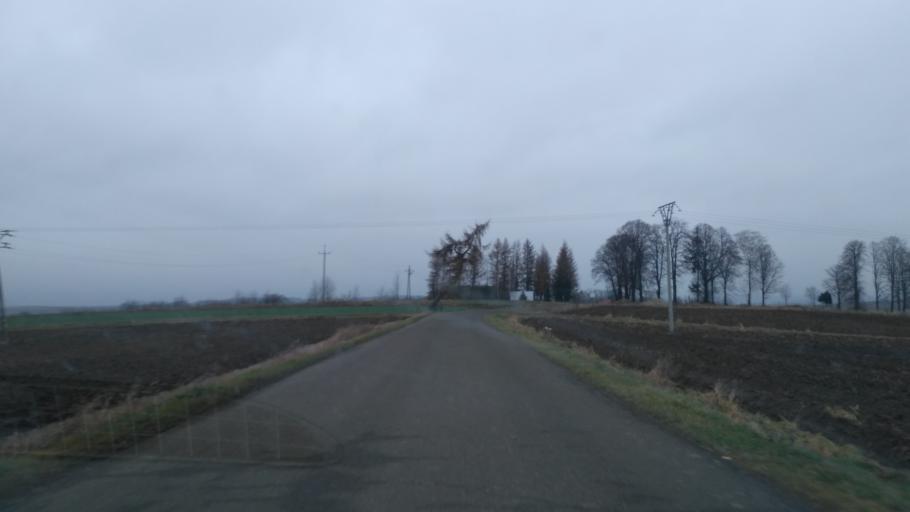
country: PL
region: Subcarpathian Voivodeship
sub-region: Powiat jaroslawski
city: Pruchnik
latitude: 49.9184
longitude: 22.5345
